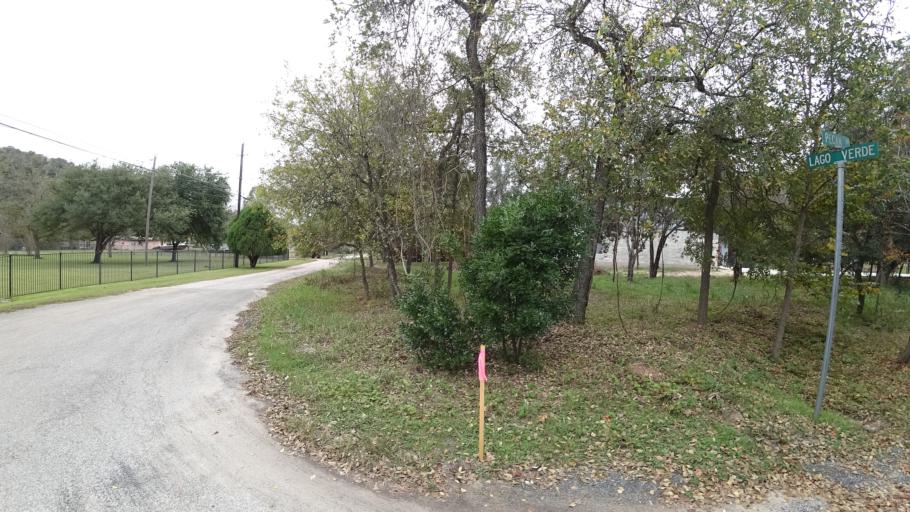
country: US
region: Texas
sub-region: Travis County
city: Bee Cave
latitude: 30.3540
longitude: -97.9191
